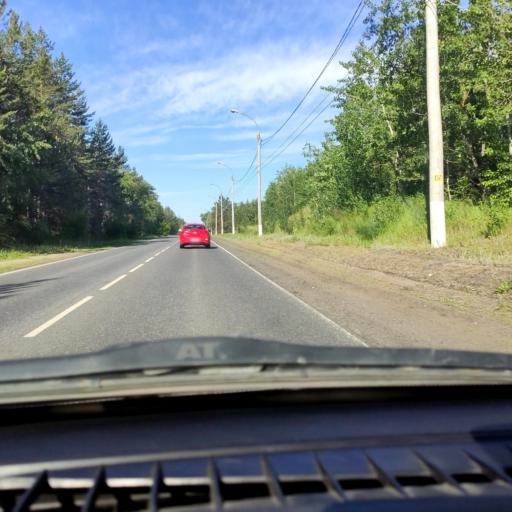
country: RU
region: Samara
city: Zhigulevsk
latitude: 53.4780
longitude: 49.4344
